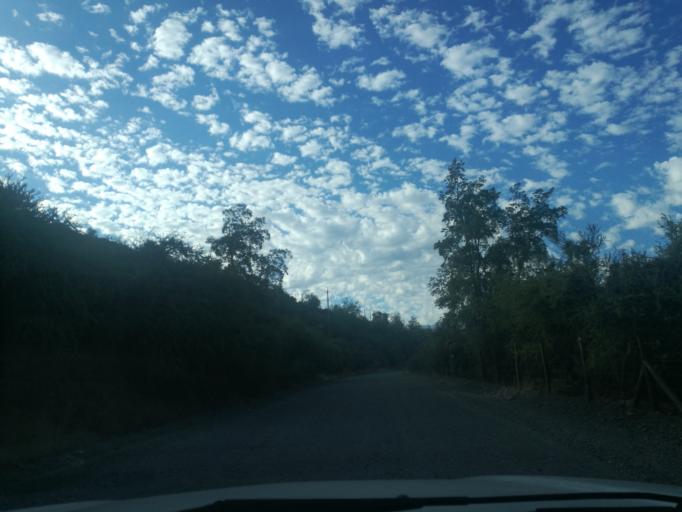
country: CL
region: O'Higgins
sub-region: Provincia de Cachapoal
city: Machali
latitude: -34.2439
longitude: -70.4700
